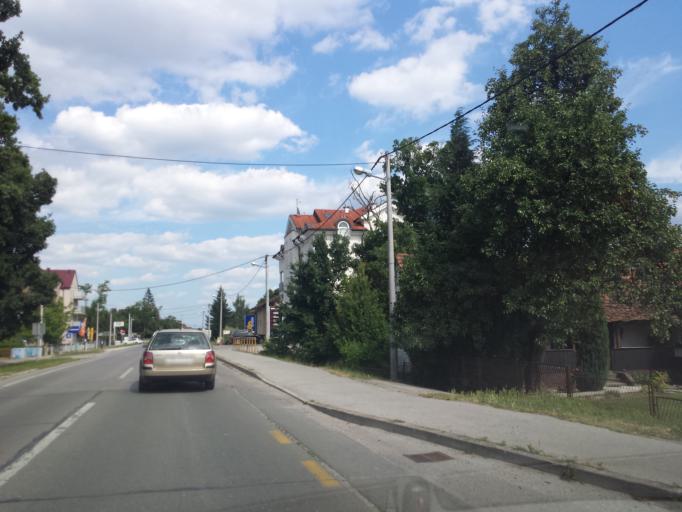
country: HR
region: Zagrebacka
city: Brckovljani
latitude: 45.8089
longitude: 16.2151
